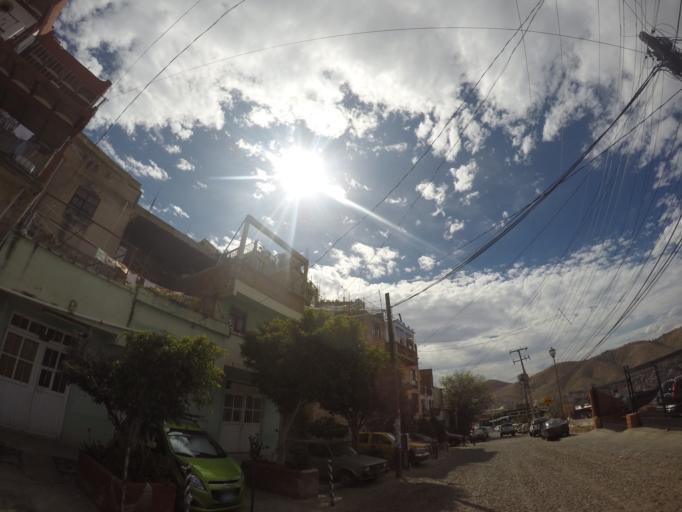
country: MX
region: Guanajuato
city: Guanajuato
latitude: 21.0157
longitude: -101.2589
